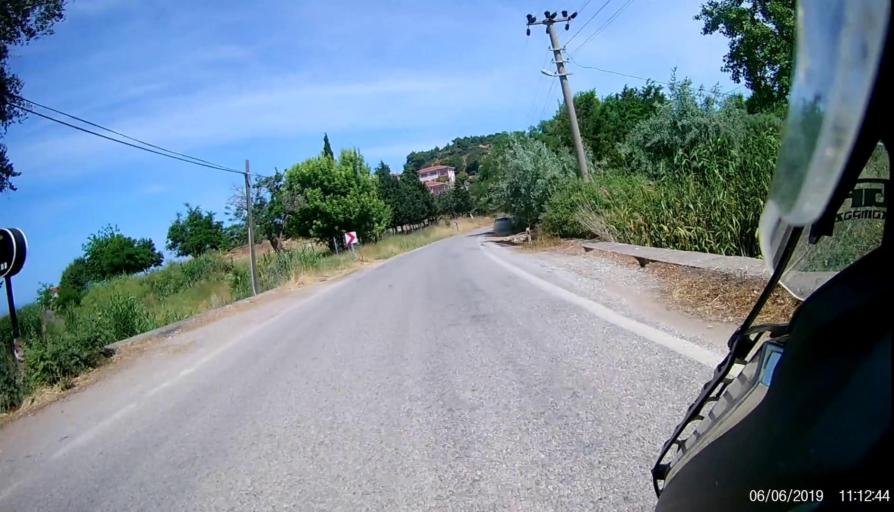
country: TR
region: Canakkale
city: Gulpinar
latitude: 39.6117
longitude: 26.1838
